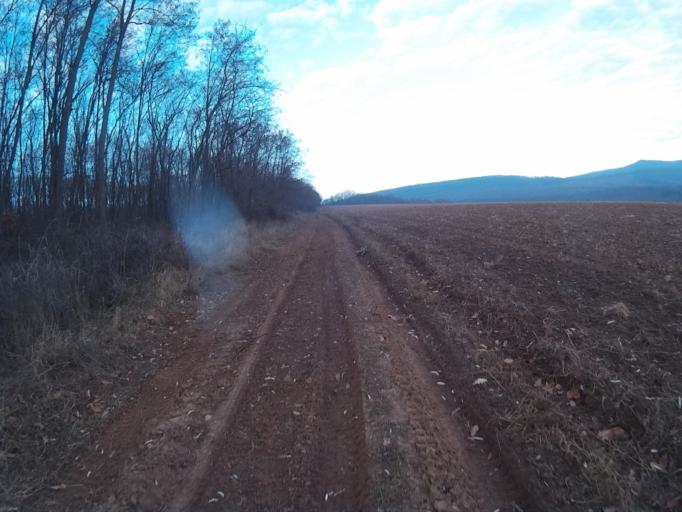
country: HU
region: Nograd
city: Rimoc
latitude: 47.9923
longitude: 19.4297
